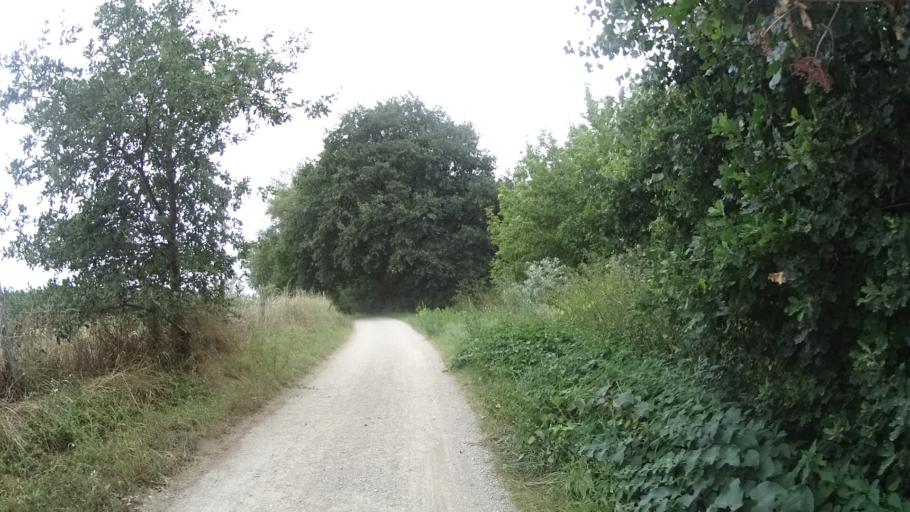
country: FR
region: Centre
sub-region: Departement du Loiret
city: Baule
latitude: 47.7928
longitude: 1.6783
